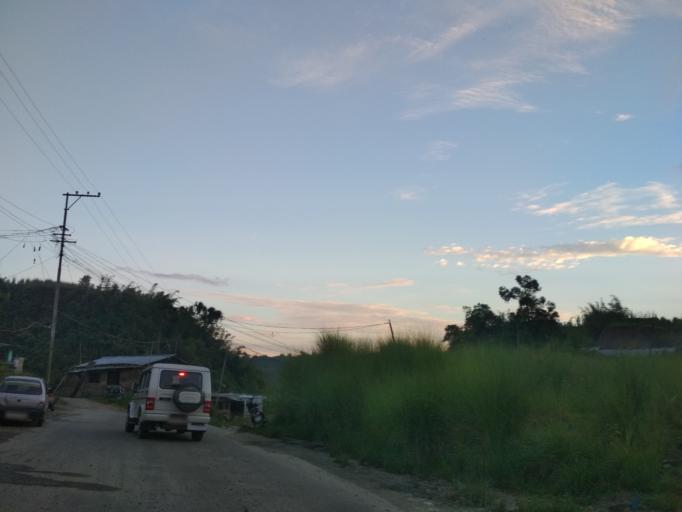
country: IN
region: Arunachal Pradesh
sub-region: Papum Pare
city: Naharlagun
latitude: 27.0967
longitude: 93.6673
